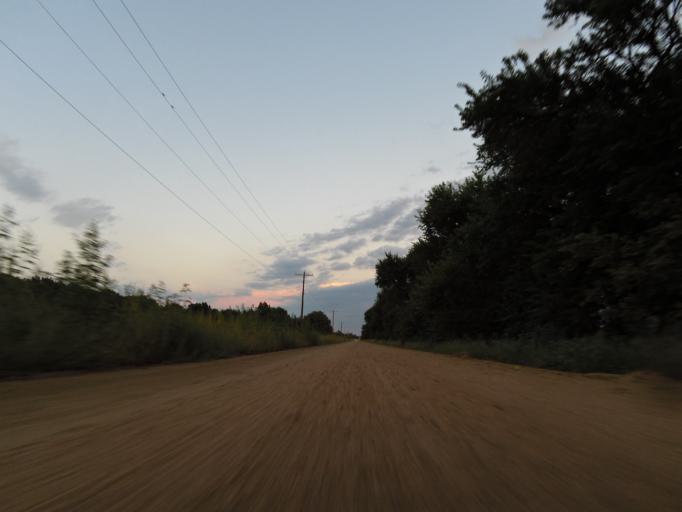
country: US
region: Kansas
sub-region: Reno County
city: South Hutchinson
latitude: 37.9556
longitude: -98.0461
